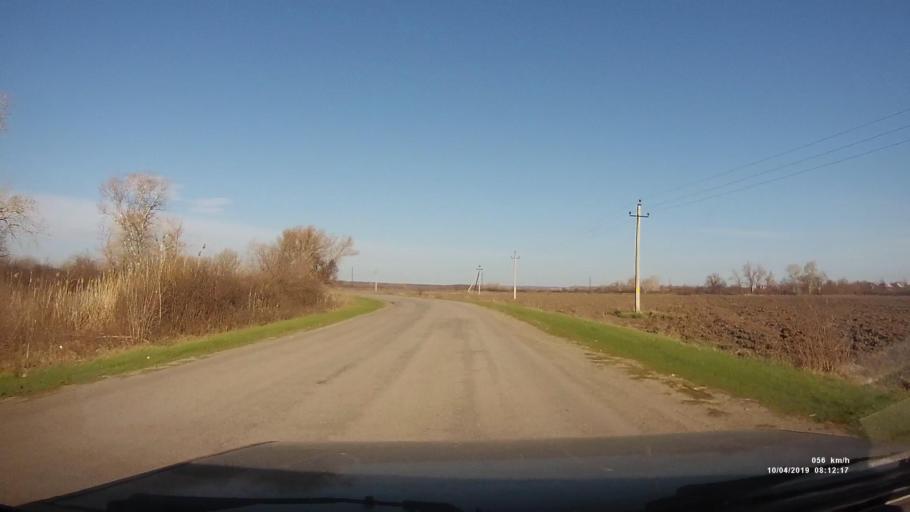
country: RU
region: Rostov
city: Masalovka
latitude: 48.3614
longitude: 40.2593
